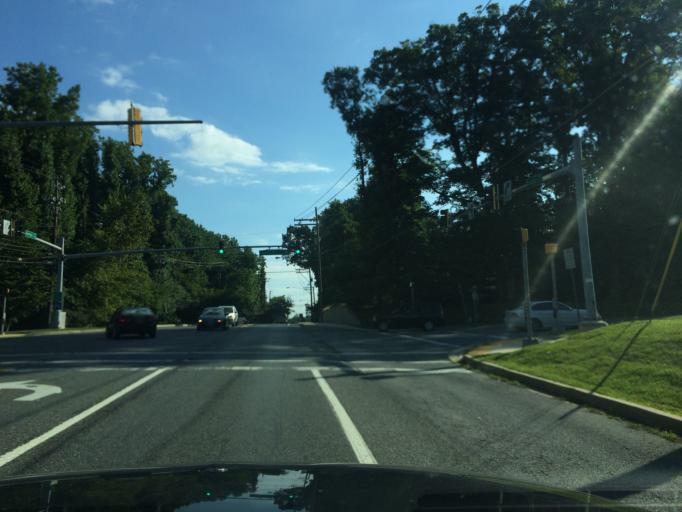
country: US
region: Maryland
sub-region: Montgomery County
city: Olney
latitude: 39.1596
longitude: -77.0642
